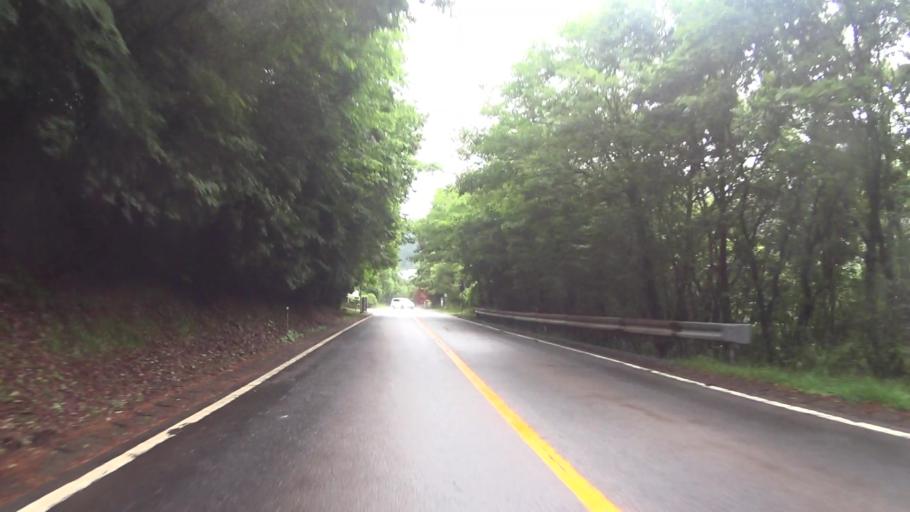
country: JP
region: Oita
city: Tsukawaki
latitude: 33.1131
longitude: 131.2265
